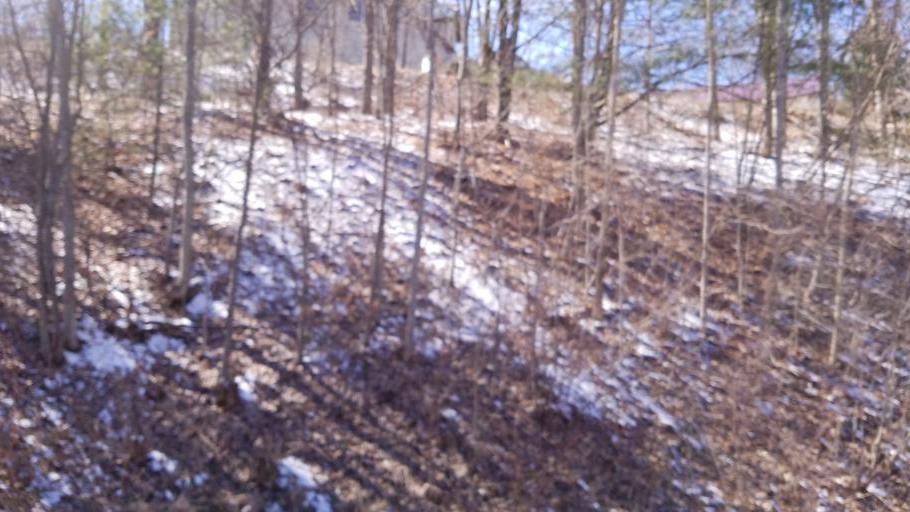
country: US
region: New York
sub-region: Allegany County
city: Wellsville
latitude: 42.0952
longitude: -77.9383
